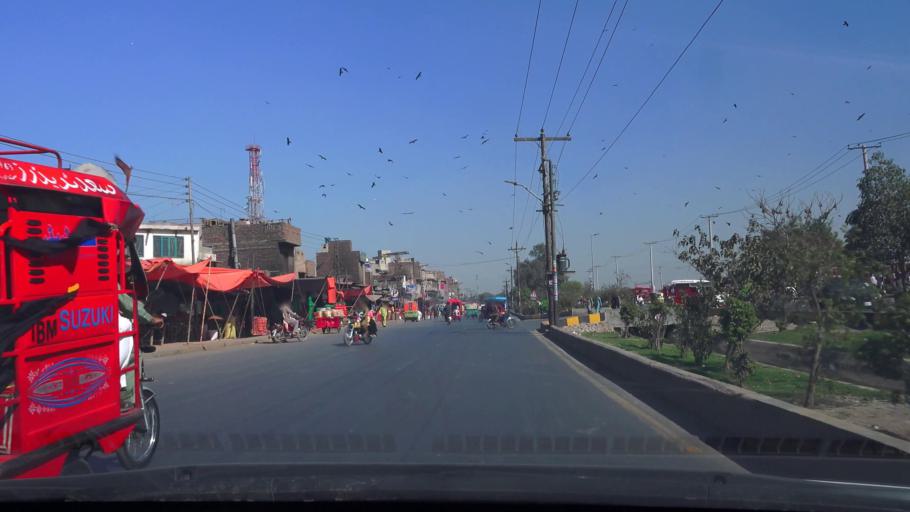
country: PK
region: Punjab
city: Faisalabad
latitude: 31.4140
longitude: 73.0727
